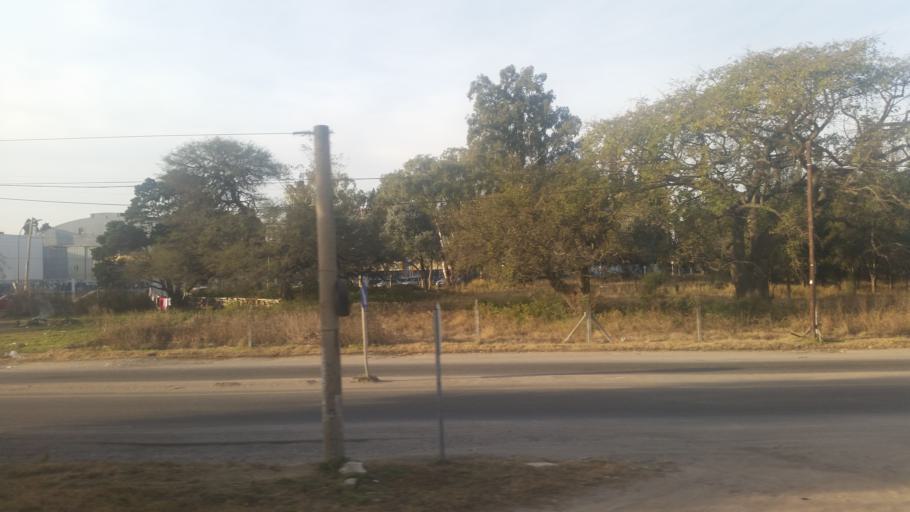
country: AR
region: Cordoba
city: Malvinas Argentinas
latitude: -31.4656
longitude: -64.1027
